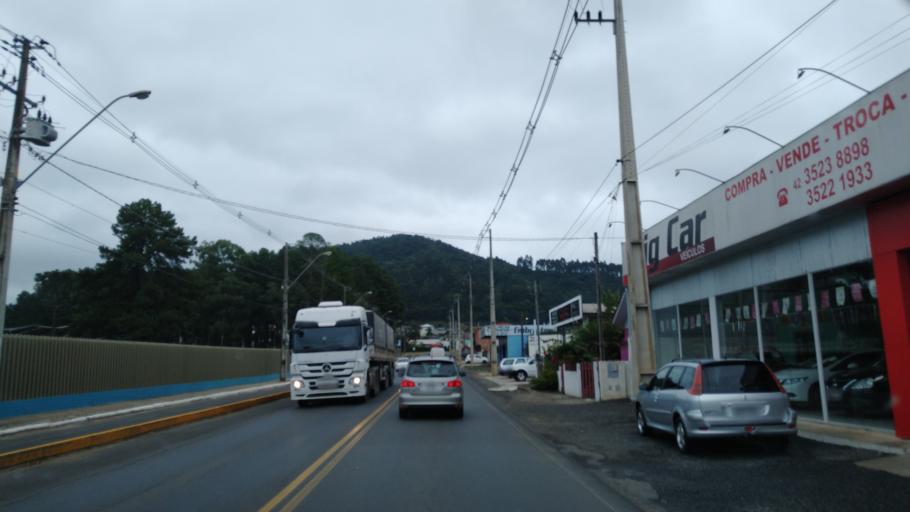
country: BR
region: Santa Catarina
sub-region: Porto Uniao
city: Porto Uniao
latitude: -26.2574
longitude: -51.0701
